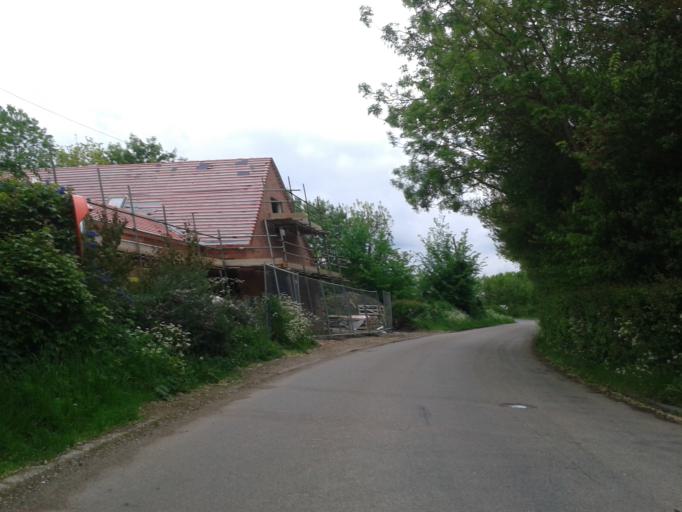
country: GB
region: England
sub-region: Northamptonshire
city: Oundle
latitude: 52.4540
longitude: -0.3973
